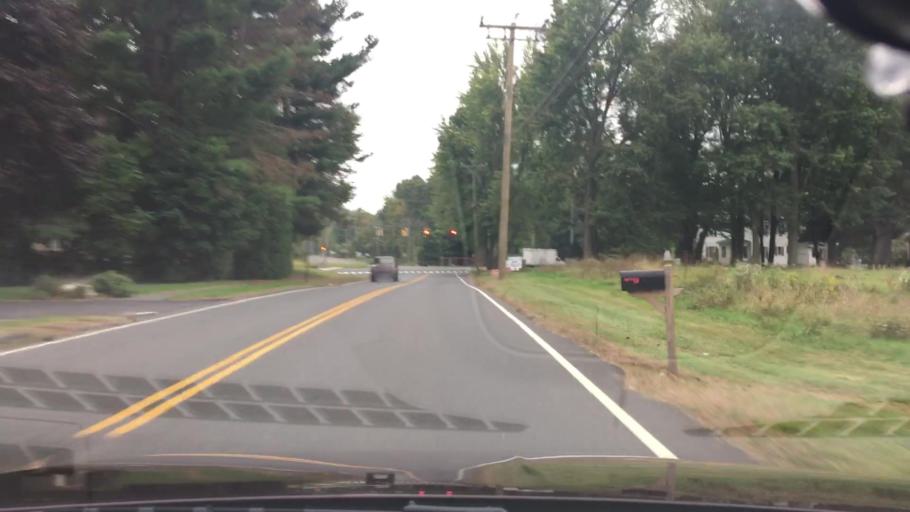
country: US
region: Connecticut
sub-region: Hartford County
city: Sherwood Manor
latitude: 42.0056
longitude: -72.5591
